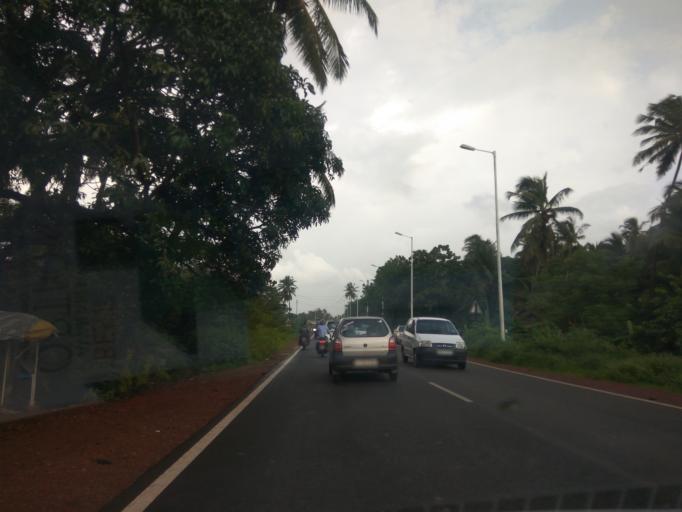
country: IN
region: Goa
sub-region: North Goa
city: Goa Velha
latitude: 15.4265
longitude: 73.8940
